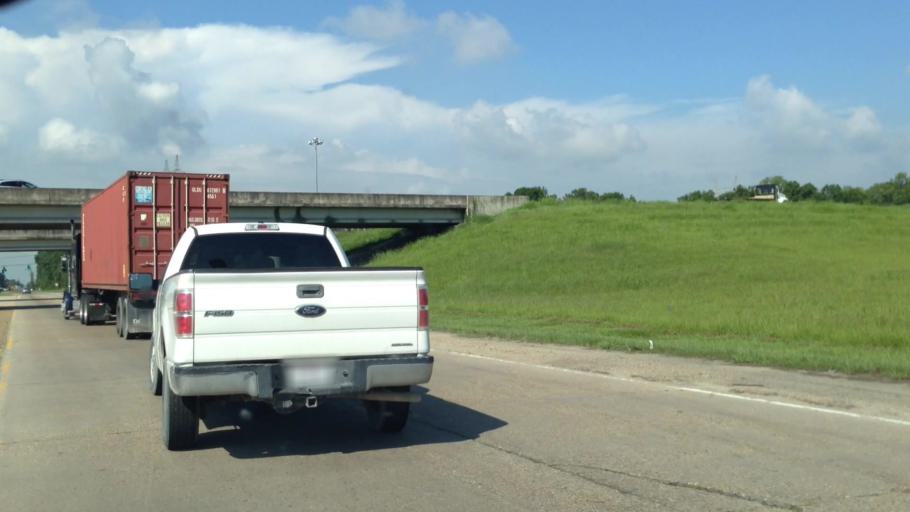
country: US
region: Louisiana
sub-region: Ascension Parish
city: Sorrento
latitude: 30.1725
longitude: -90.8762
